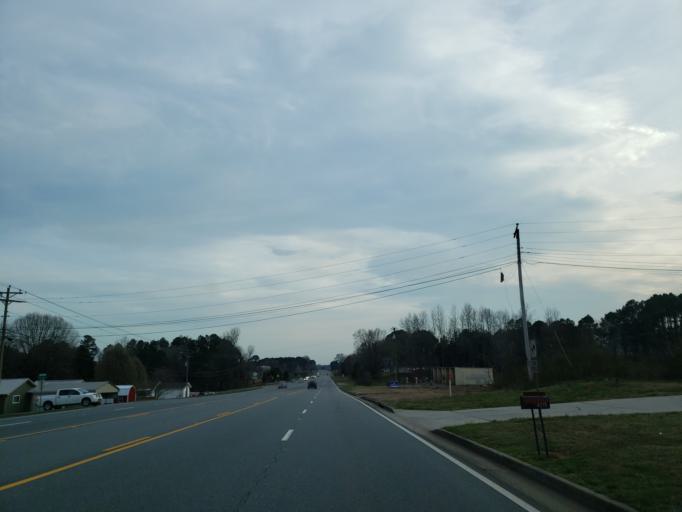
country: US
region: Georgia
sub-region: Whitfield County
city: Varnell
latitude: 34.9109
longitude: -84.9461
